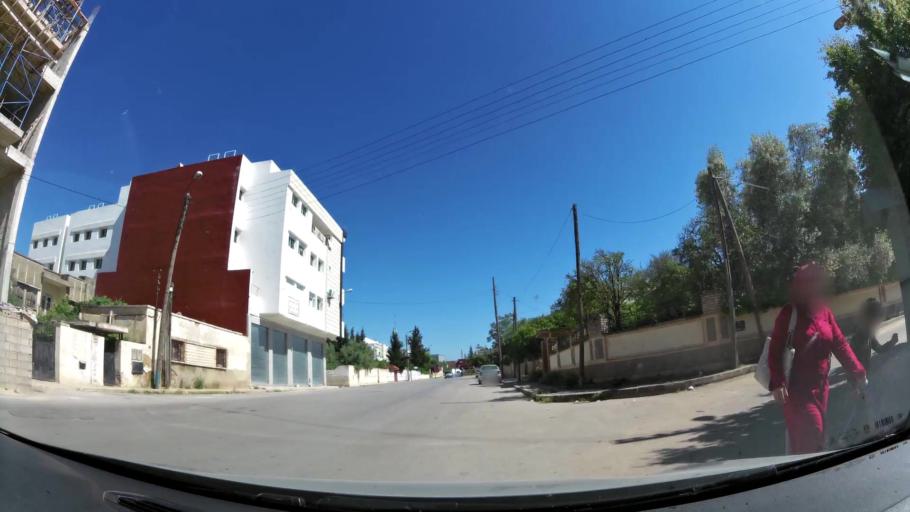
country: MA
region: Fes-Boulemane
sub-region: Fes
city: Fes
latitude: 34.0190
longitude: -4.9924
